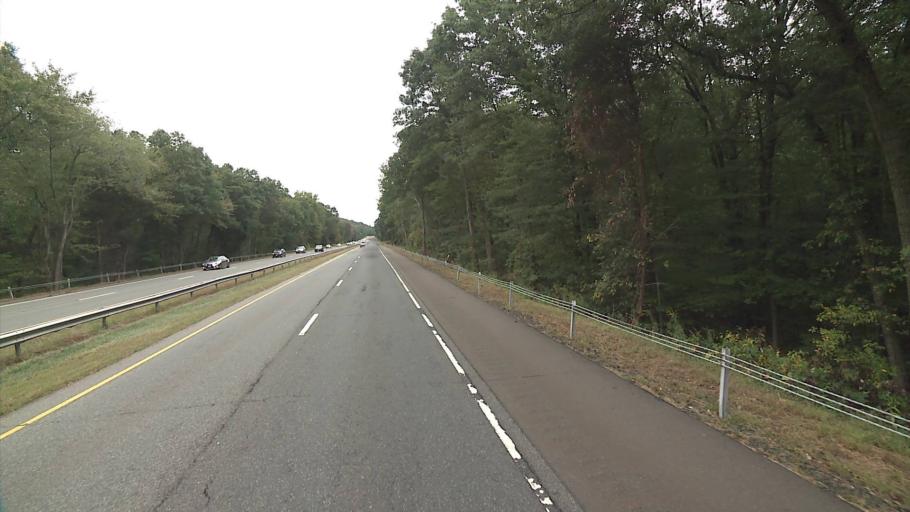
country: US
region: Connecticut
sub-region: New Haven County
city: North Haven
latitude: 41.4199
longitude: -72.8554
